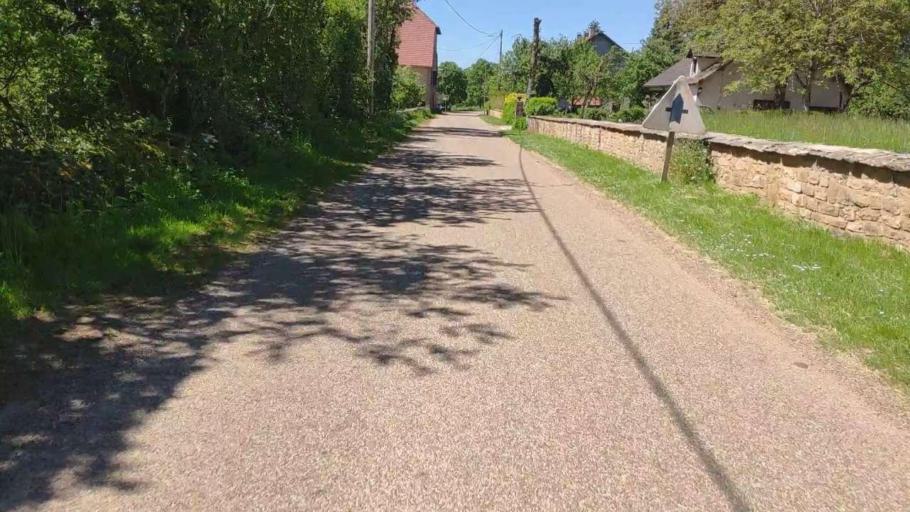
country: FR
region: Franche-Comte
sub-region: Departement du Jura
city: Poligny
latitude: 46.7283
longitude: 5.7502
